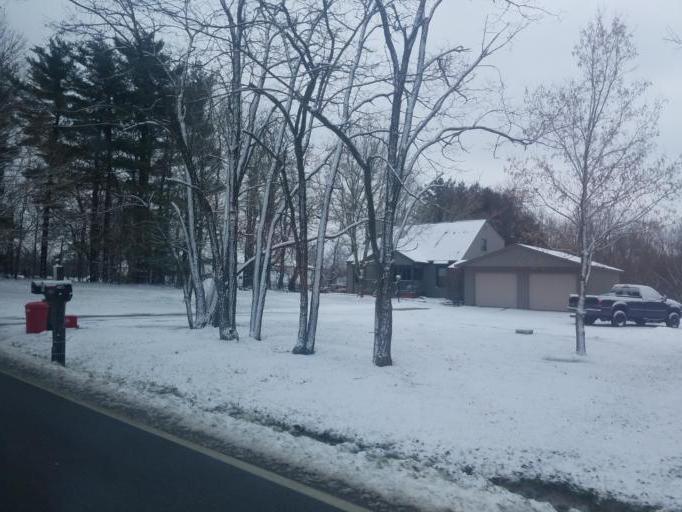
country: US
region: Ohio
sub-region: Franklin County
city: New Albany
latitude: 40.0957
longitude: -82.7644
